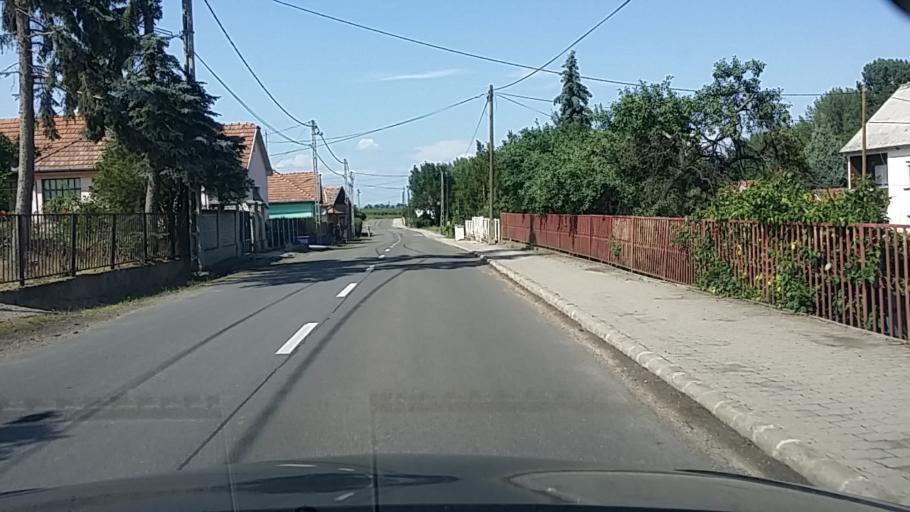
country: SK
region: Nitriansky
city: Sahy
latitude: 48.0241
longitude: 18.8969
